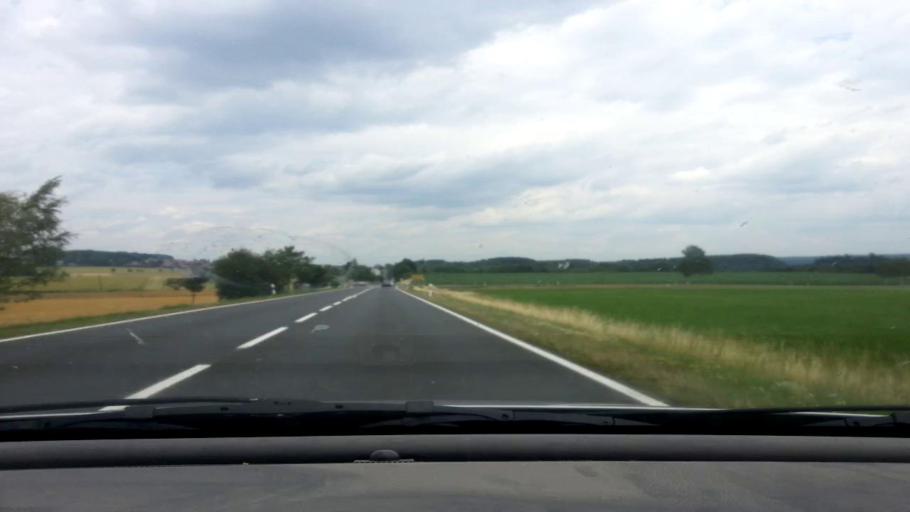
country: DE
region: Bavaria
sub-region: Upper Palatinate
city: Mitterteich
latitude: 49.9666
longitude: 12.2593
